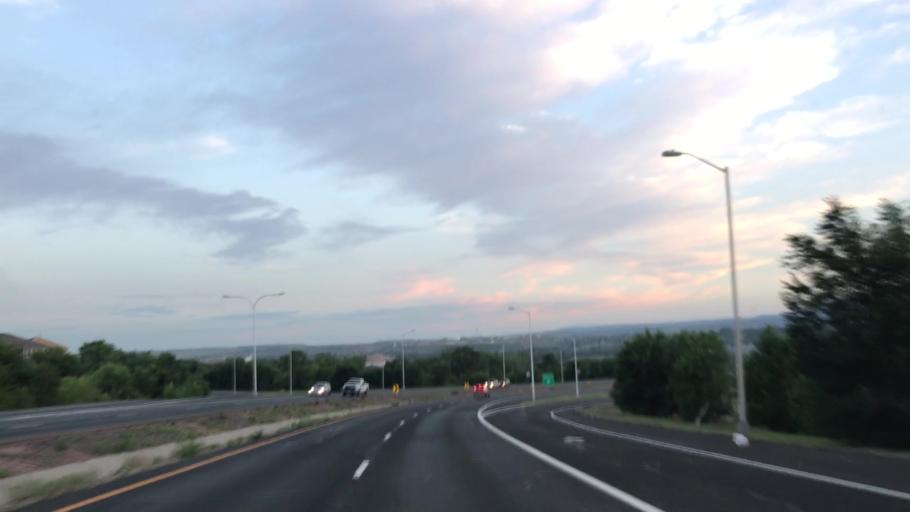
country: US
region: Colorado
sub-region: El Paso County
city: Stratmoor
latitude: 38.8023
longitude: -104.7804
